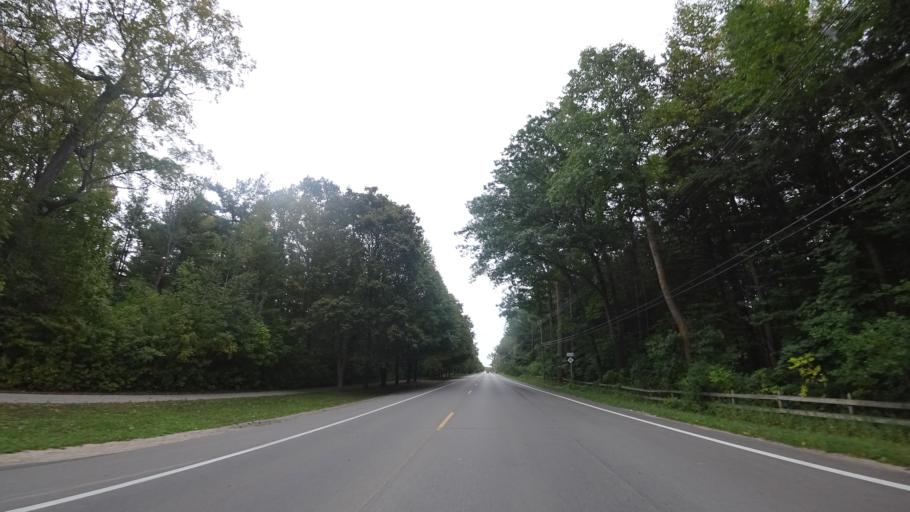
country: US
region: Michigan
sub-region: Emmet County
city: Harbor Springs
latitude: 45.4315
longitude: -84.9557
